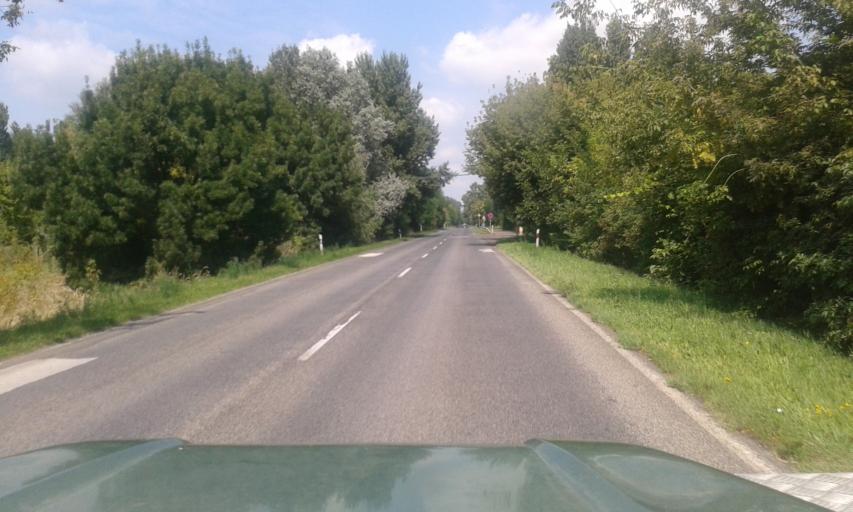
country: HU
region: Csongrad
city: Szatymaz
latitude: 46.3292
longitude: 20.0640
